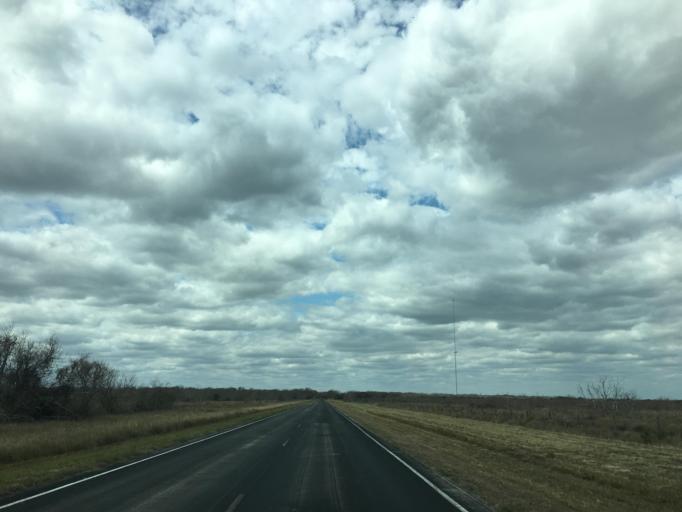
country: US
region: Texas
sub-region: Brazoria County
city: Oyster Creek
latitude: 29.0653
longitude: -95.3099
